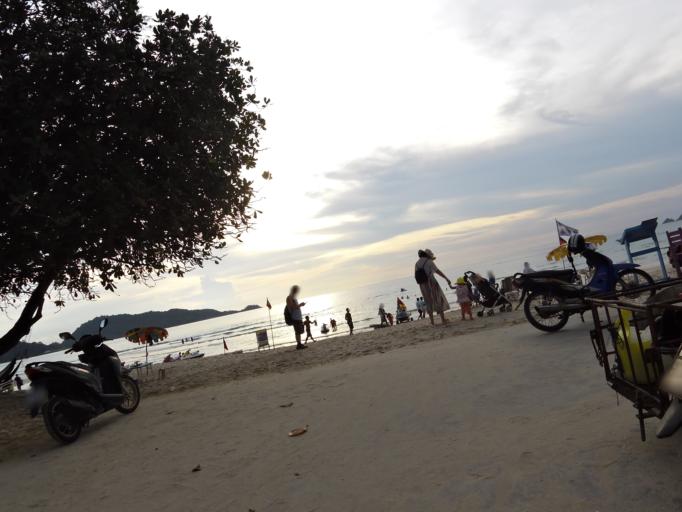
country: TH
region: Phuket
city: Patong
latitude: 7.8979
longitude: 98.2961
